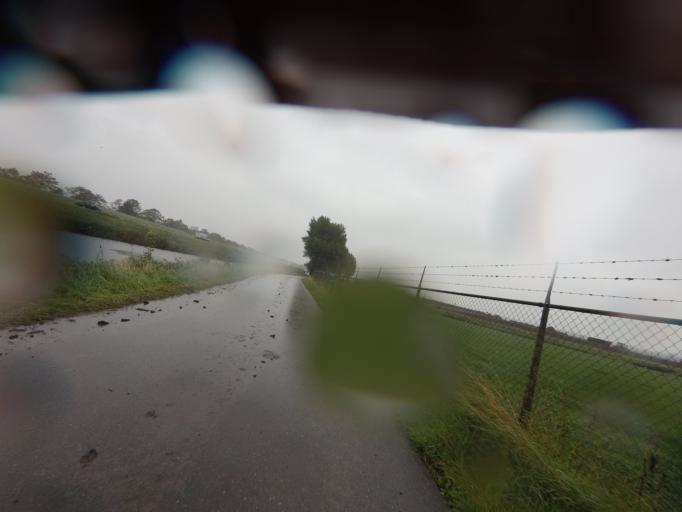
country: NL
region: North Holland
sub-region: Gemeente Medemblik
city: Opperdoes
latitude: 52.7522
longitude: 5.0451
